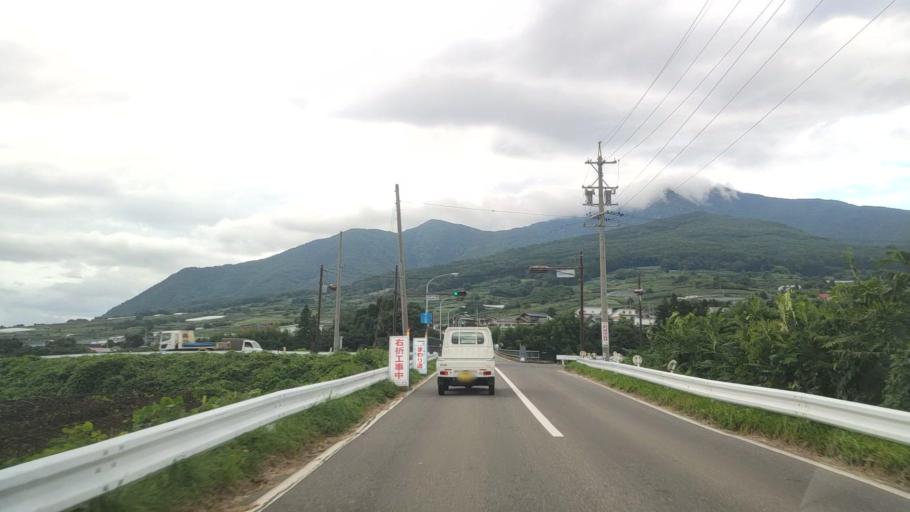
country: JP
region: Nagano
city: Nakano
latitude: 36.7726
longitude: 138.3758
